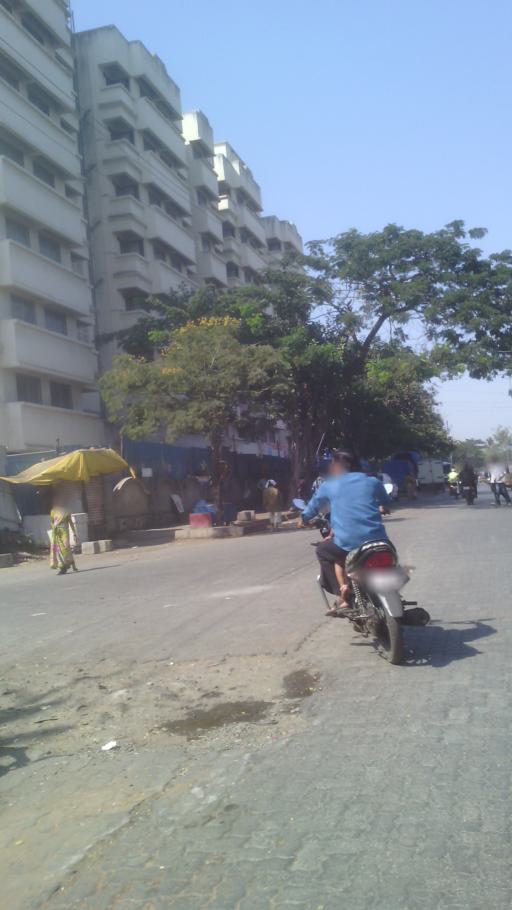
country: IN
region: Maharashtra
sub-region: Thane
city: Kalyan
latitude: 19.2443
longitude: 73.1519
